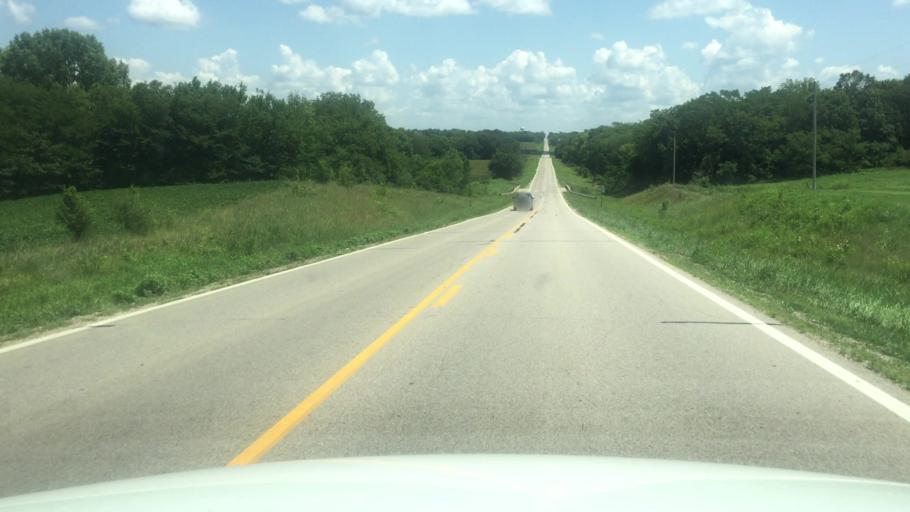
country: US
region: Kansas
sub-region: Brown County
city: Horton
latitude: 39.6674
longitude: -95.5617
